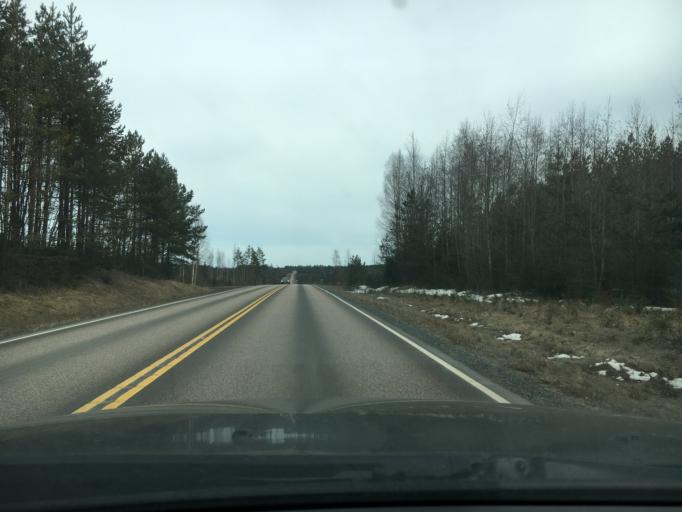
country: FI
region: Central Finland
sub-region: AEaenekoski
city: Konnevesi
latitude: 62.6880
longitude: 26.3994
